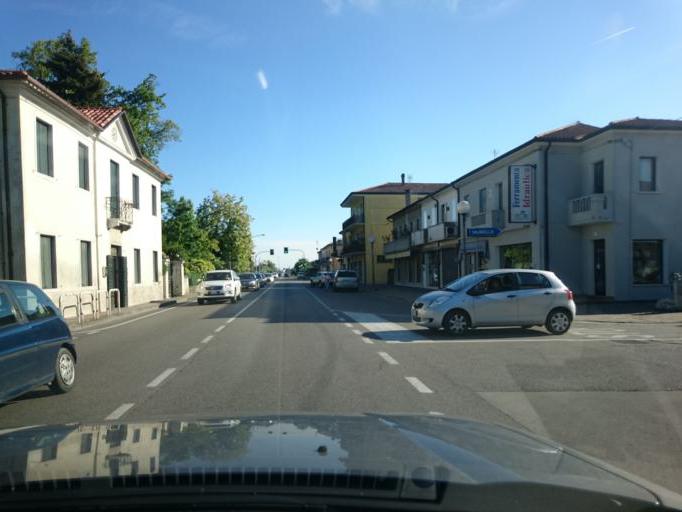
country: IT
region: Veneto
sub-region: Provincia di Venezia
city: Caselle
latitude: 45.4903
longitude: 12.0058
